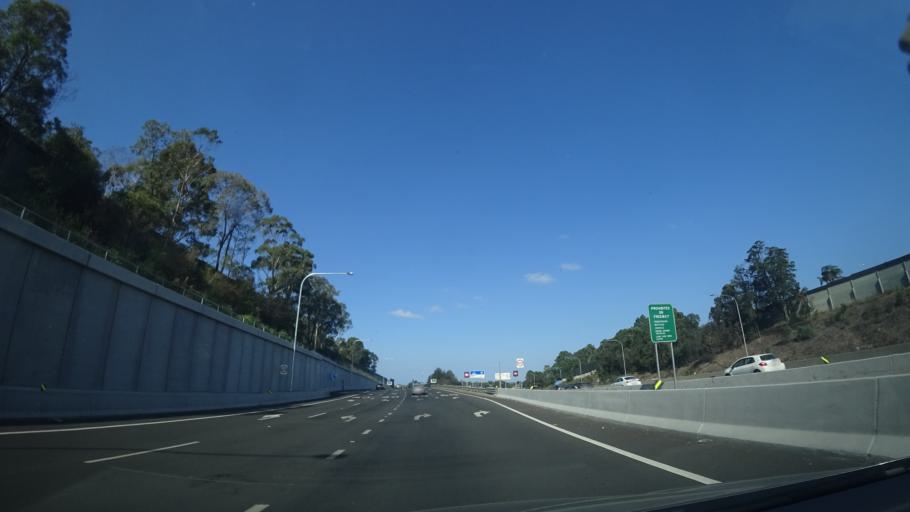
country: AU
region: New South Wales
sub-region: Canterbury
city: Roselands
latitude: -33.9435
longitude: 151.0739
